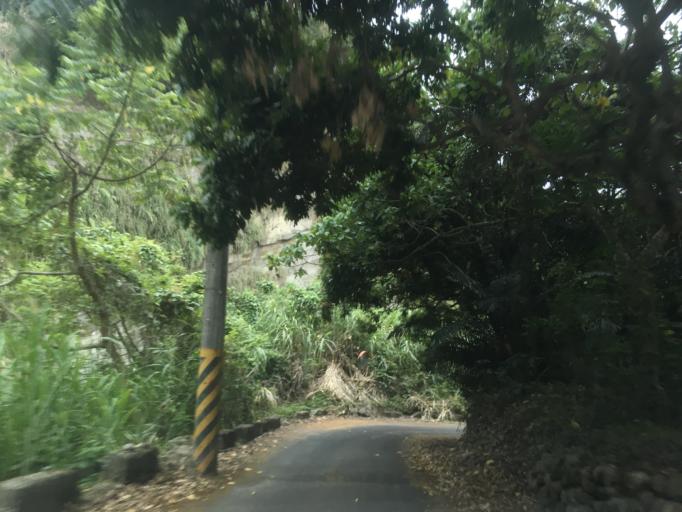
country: TW
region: Taiwan
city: Zhongxing New Village
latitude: 24.0370
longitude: 120.7591
